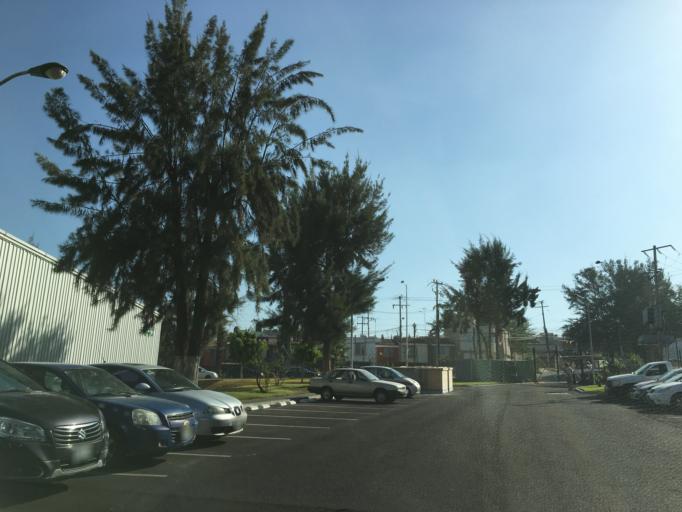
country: MX
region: Jalisco
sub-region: Tlajomulco de Zuniga
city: La Tijera
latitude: 20.6157
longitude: -103.4178
